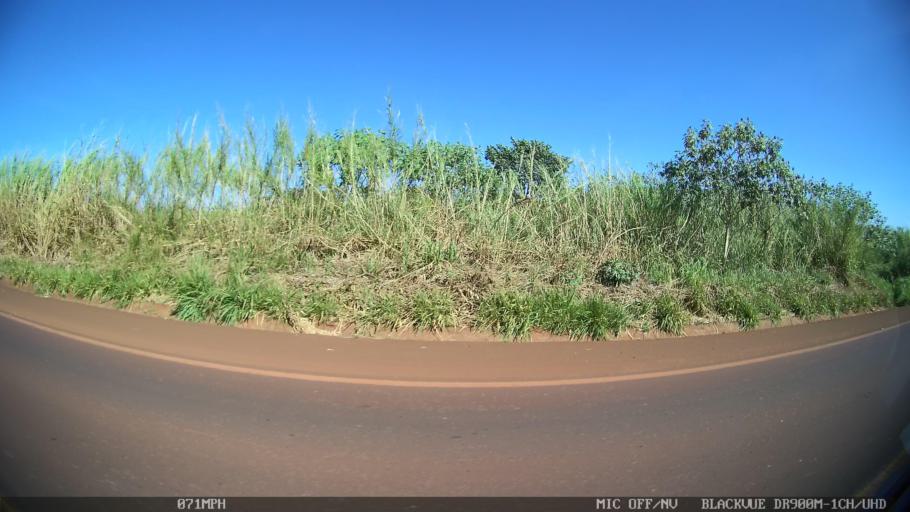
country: BR
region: Sao Paulo
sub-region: Ipua
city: Ipua
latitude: -20.4913
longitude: -48.0524
